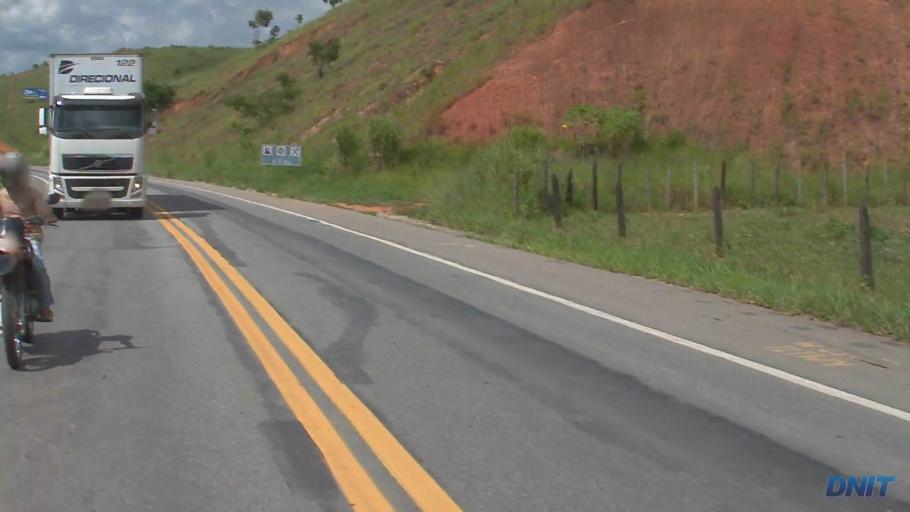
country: BR
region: Minas Gerais
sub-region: Governador Valadares
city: Governador Valadares
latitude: -19.0424
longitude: -42.1500
